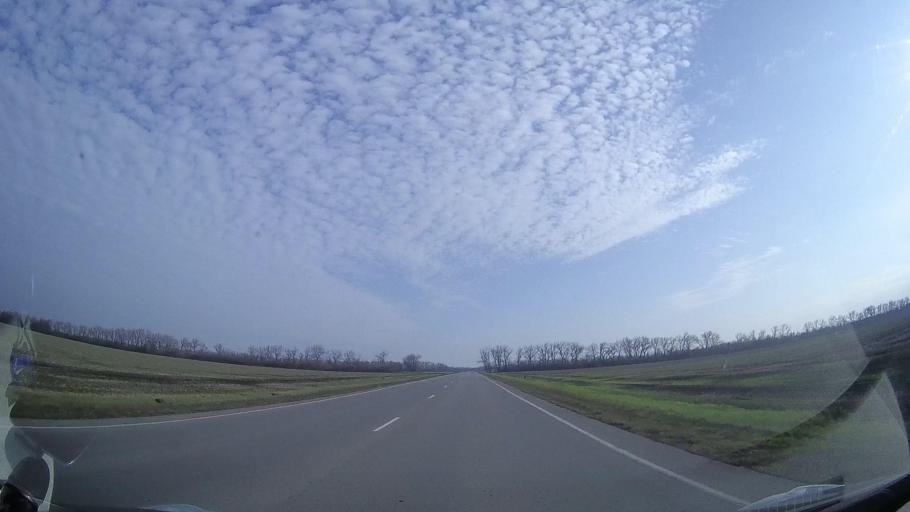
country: RU
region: Rostov
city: Tselina
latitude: 46.5228
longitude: 41.1305
